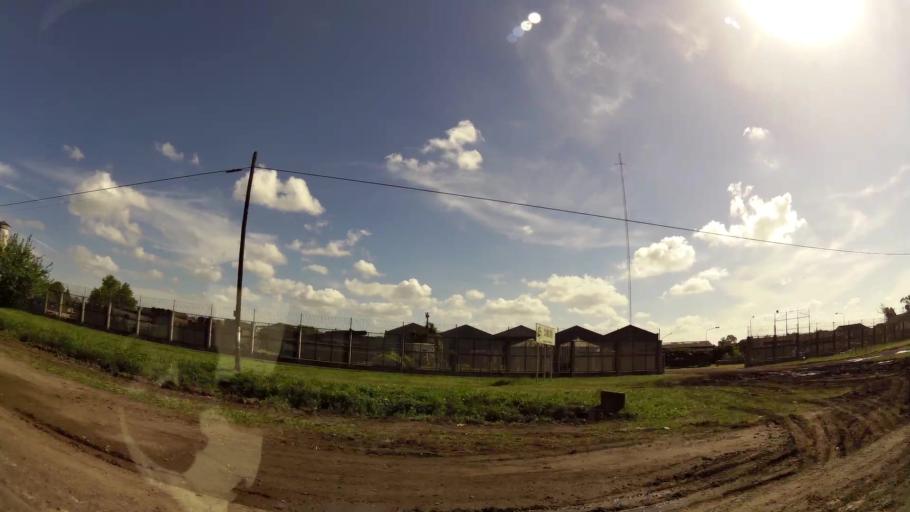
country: AR
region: Buenos Aires
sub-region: Partido de Quilmes
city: Quilmes
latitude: -34.7959
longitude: -58.2448
